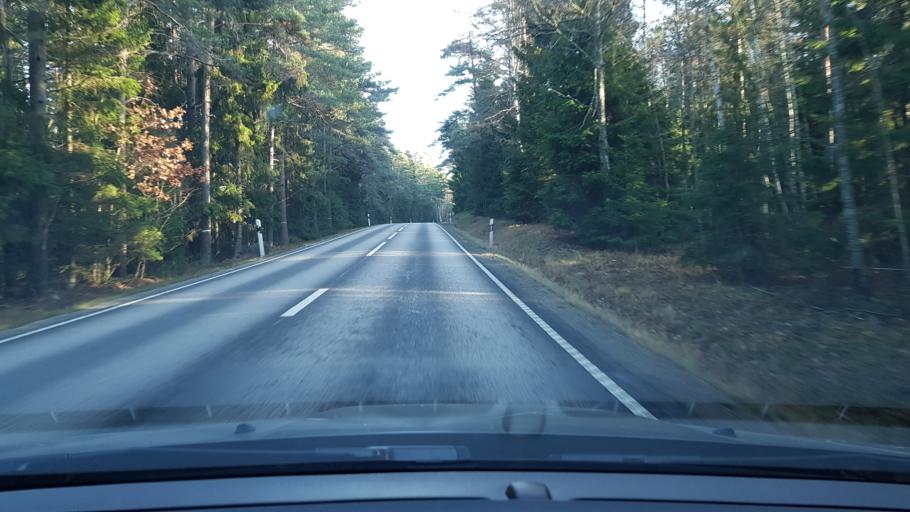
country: SE
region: Stockholm
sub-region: Norrtalje Kommun
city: Nykvarn
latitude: 59.7414
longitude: 18.2191
